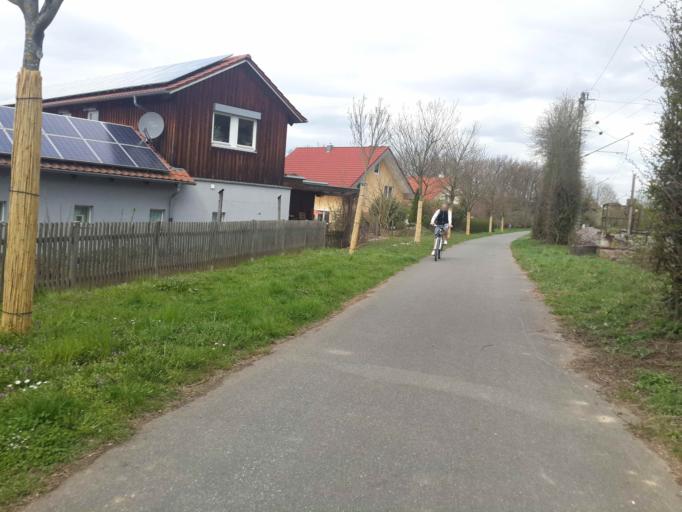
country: DE
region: Baden-Wuerttemberg
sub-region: Regierungsbezirk Stuttgart
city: Untereisesheim
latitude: 49.2385
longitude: 9.1907
